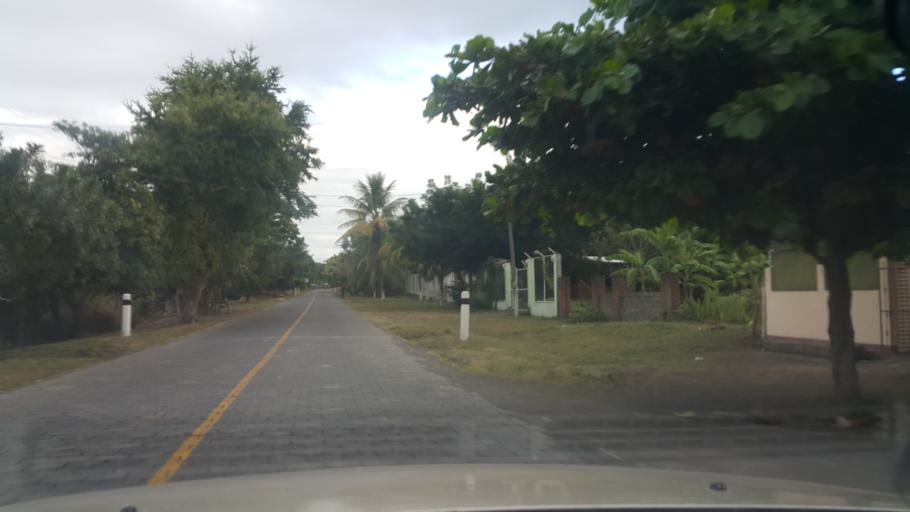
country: NI
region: Rivas
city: Moyogalpa
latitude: 11.5326
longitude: -85.6980
